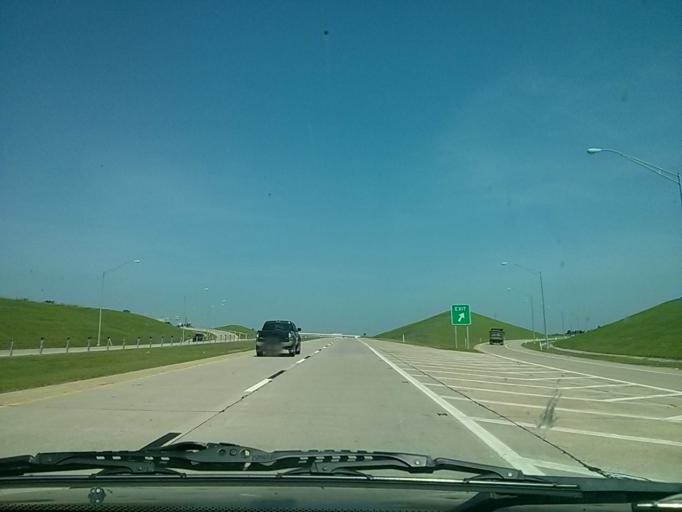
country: US
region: Oklahoma
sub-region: Tulsa County
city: Glenpool
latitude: 36.0102
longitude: -96.0410
